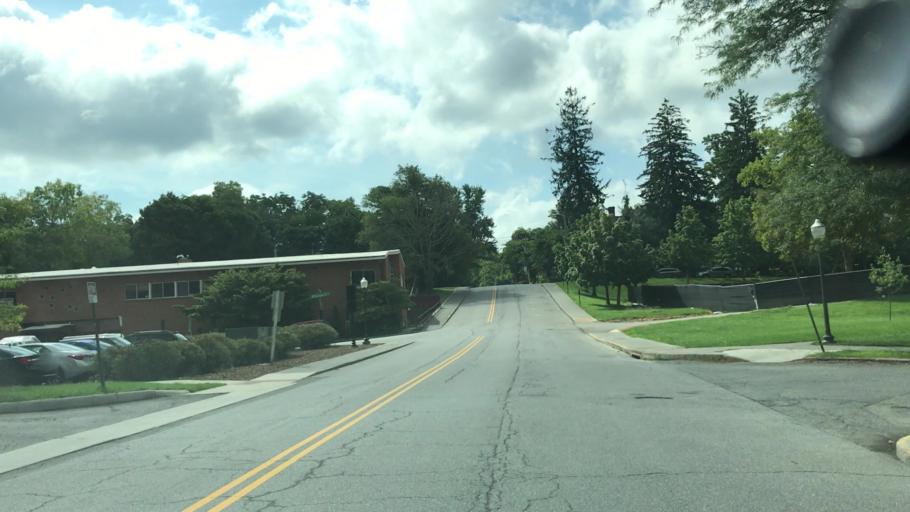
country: US
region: Virginia
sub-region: Montgomery County
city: Blacksburg
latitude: 37.2282
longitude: -80.4167
